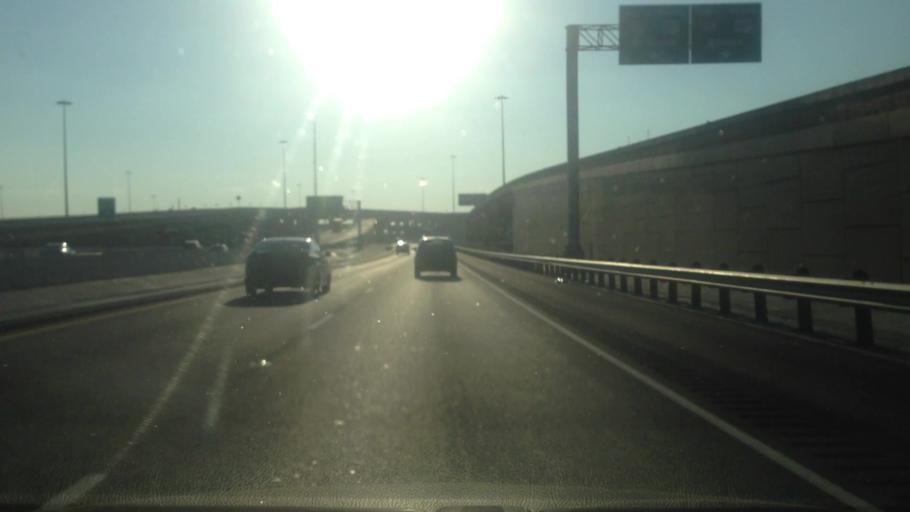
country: US
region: Texas
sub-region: Tarrant County
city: Blue Mound
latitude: 32.8375
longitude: -97.3043
